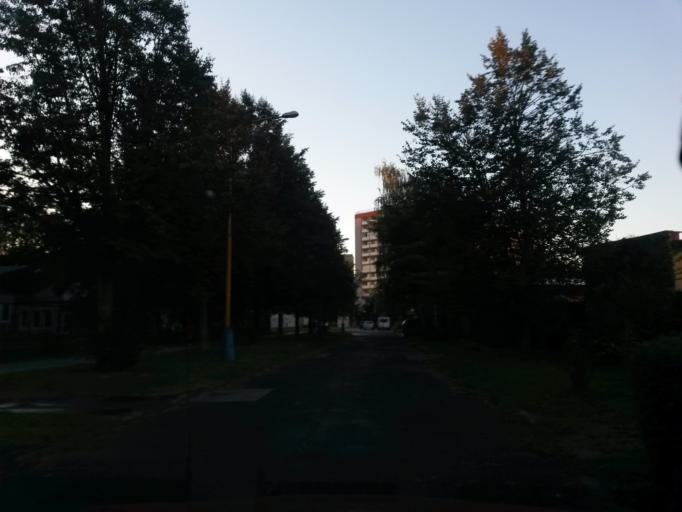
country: SK
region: Kosicky
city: Kosice
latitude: 48.6894
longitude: 21.2868
